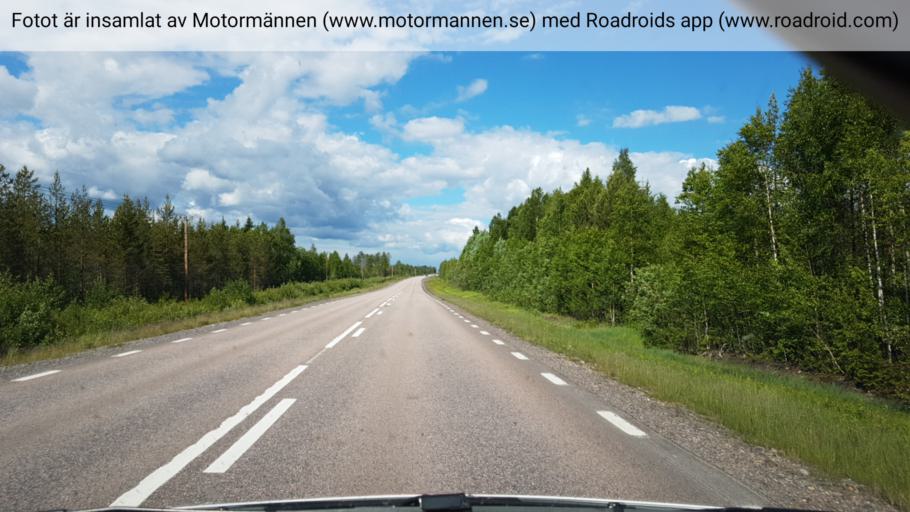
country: SE
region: Norrbotten
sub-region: Kalix Kommun
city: Toere
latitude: 66.0132
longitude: 22.6992
